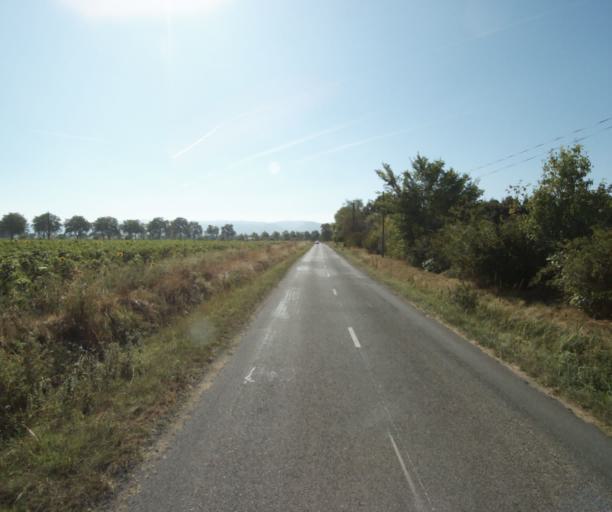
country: FR
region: Midi-Pyrenees
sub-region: Departement de la Haute-Garonne
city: Revel
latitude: 43.4795
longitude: 2.0100
